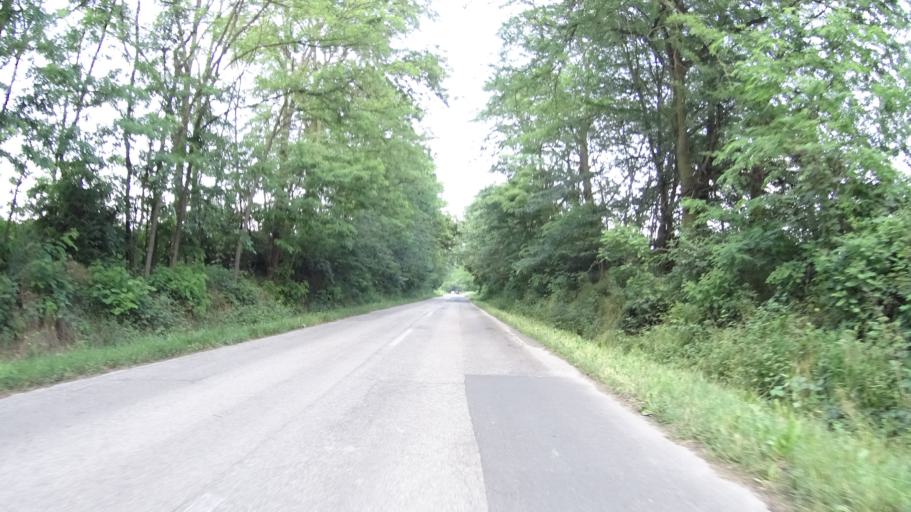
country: HU
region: Pest
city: Dunabogdany
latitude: 47.7971
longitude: 19.0576
